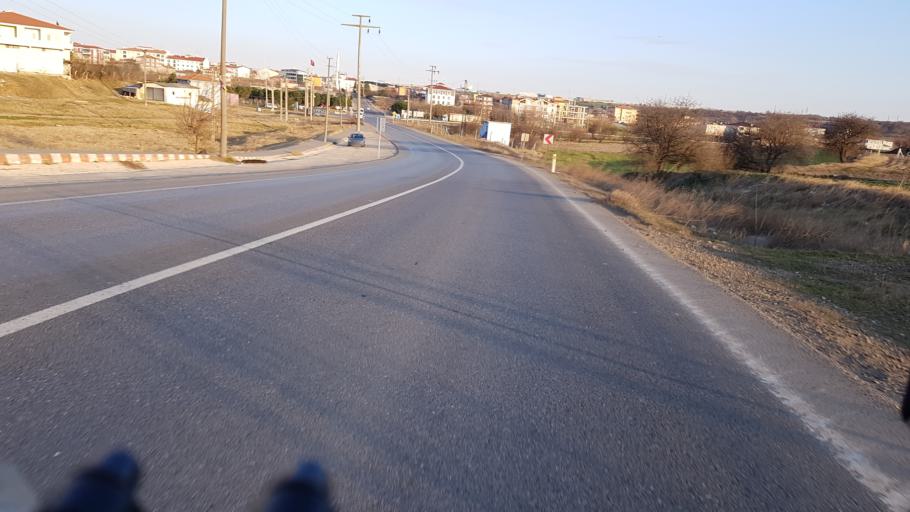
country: TR
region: Tekirdag
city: Velimese
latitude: 41.2504
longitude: 27.8706
